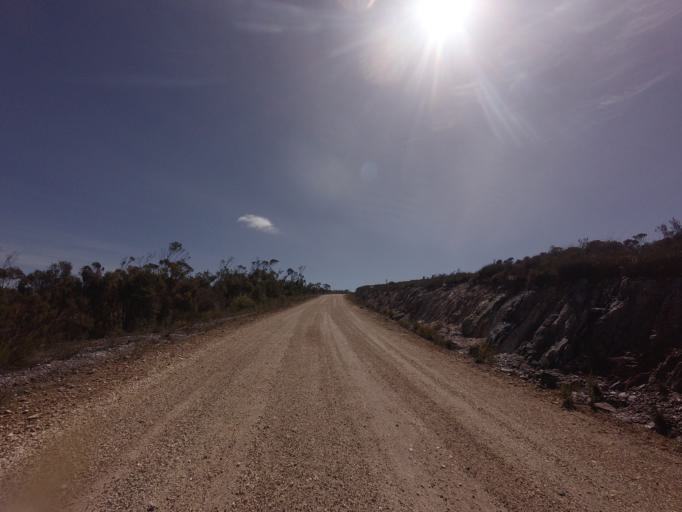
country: AU
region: Tasmania
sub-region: Huon Valley
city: Geeveston
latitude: -43.0389
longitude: 146.2742
